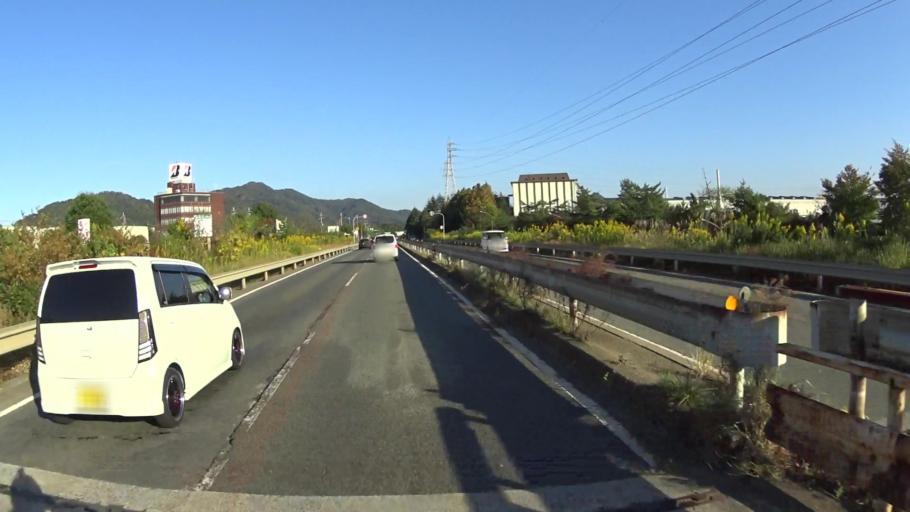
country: JP
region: Kyoto
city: Fukuchiyama
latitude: 35.2880
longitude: 135.1727
